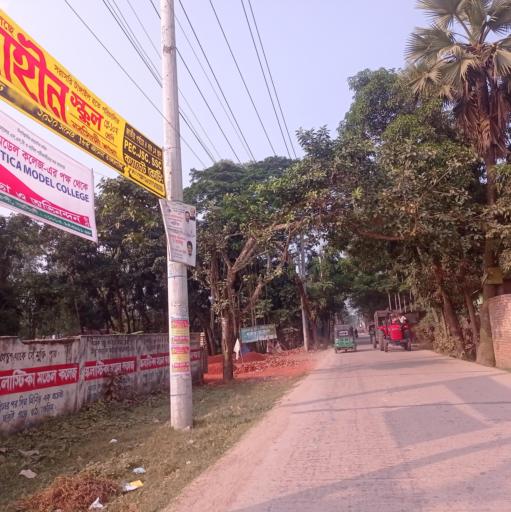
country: BD
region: Dhaka
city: Bhairab Bazar
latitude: 24.0991
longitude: 90.8528
